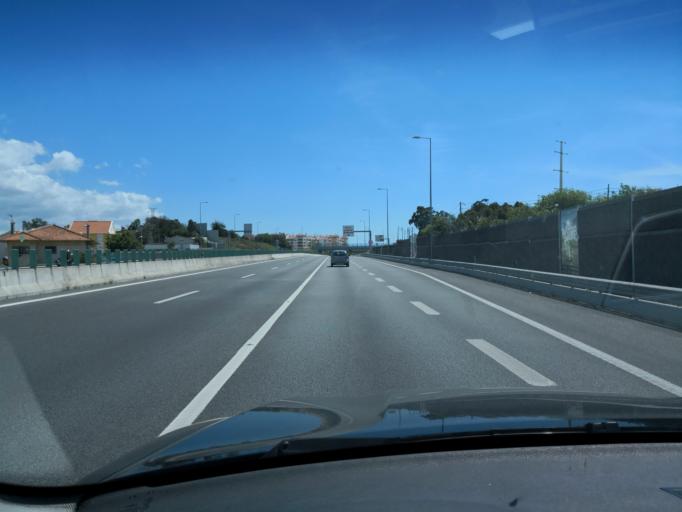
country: PT
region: Setubal
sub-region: Almada
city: Sobreda
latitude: 38.6510
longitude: -9.2009
